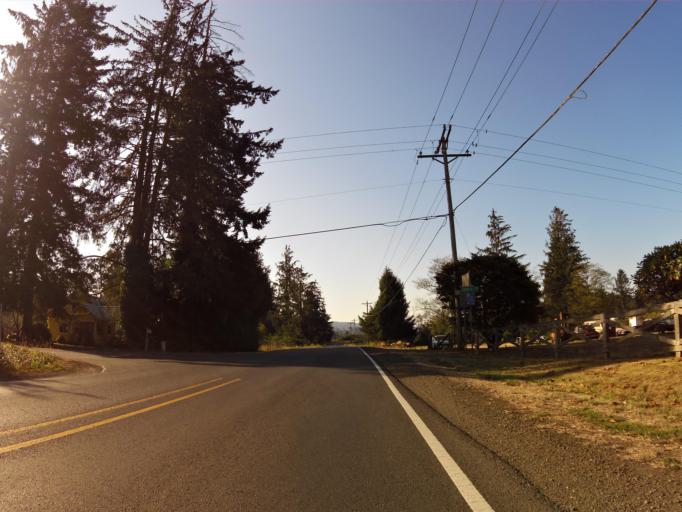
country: US
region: Oregon
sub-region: Tillamook County
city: Tillamook
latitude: 45.4305
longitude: -123.7779
